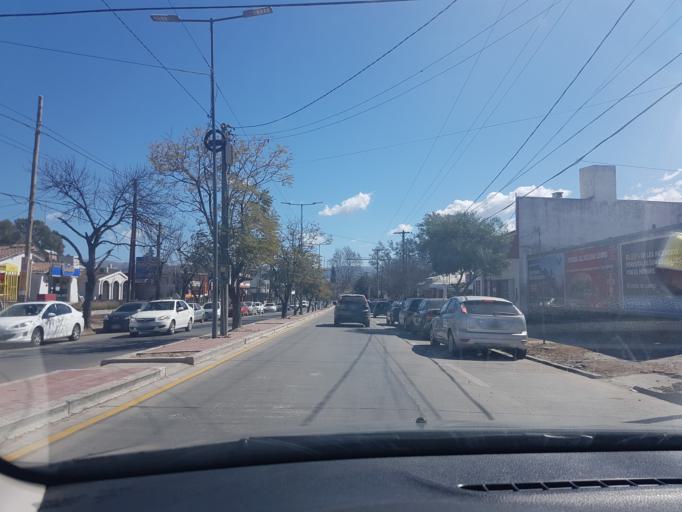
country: AR
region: Cordoba
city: Villa Allende
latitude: -31.2987
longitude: -64.2895
